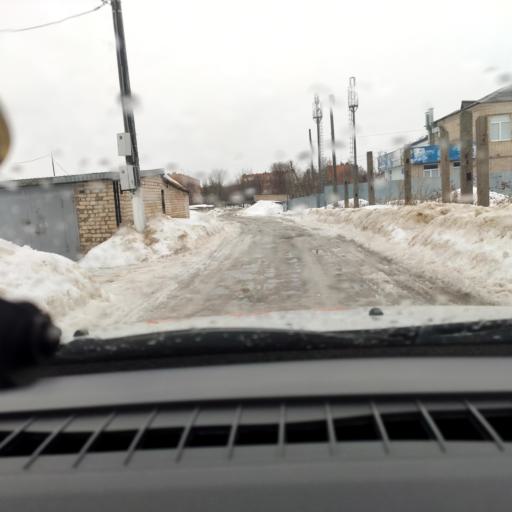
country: RU
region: Samara
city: Chapayevsk
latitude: 52.9902
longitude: 49.7779
